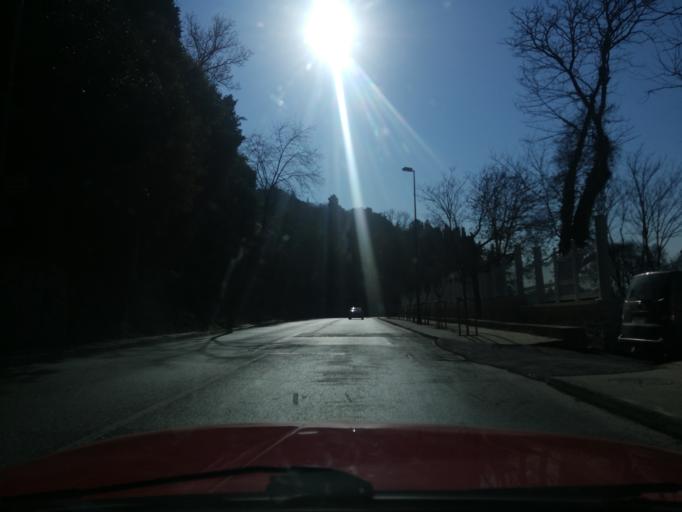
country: TR
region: Istanbul
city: UEskuedar
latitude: 41.0760
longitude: 29.0658
